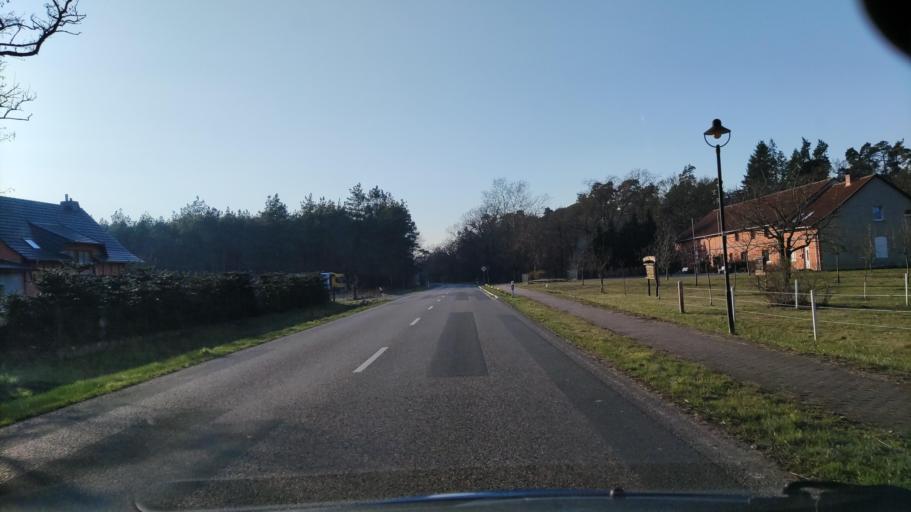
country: DE
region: Saxony-Anhalt
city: Seehausen
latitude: 52.9221
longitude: 11.6968
